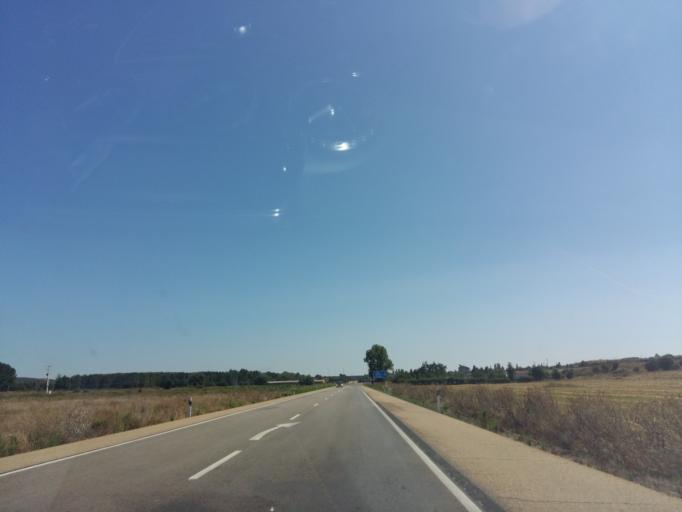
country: ES
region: Castille and Leon
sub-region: Provincia de Leon
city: Astorga
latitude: 42.4436
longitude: -6.0429
